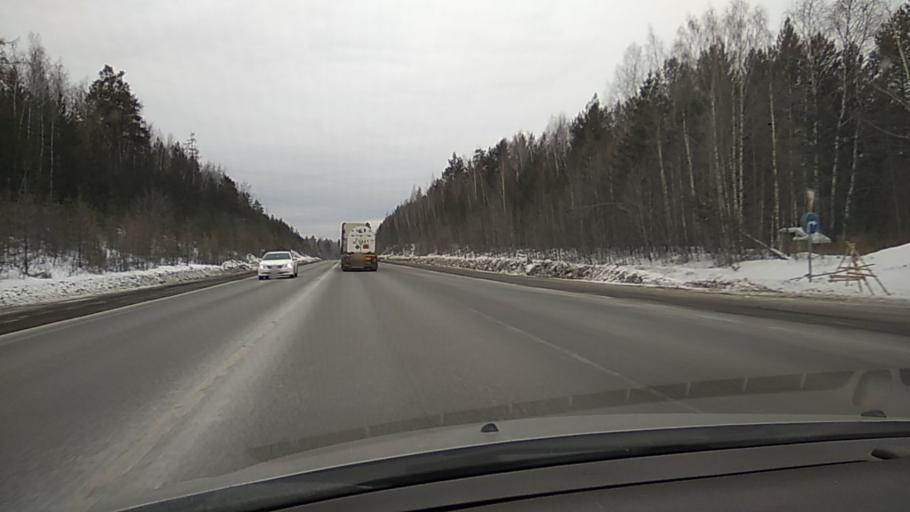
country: RU
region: Sverdlovsk
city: Talitsa
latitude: 56.8344
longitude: 59.9983
